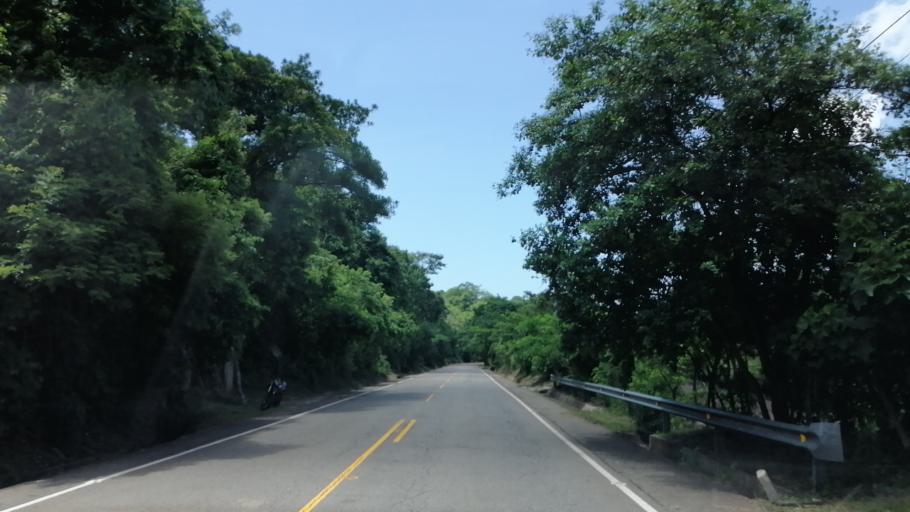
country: SV
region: Chalatenango
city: Nueva Concepcion
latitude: 14.1780
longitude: -89.3200
